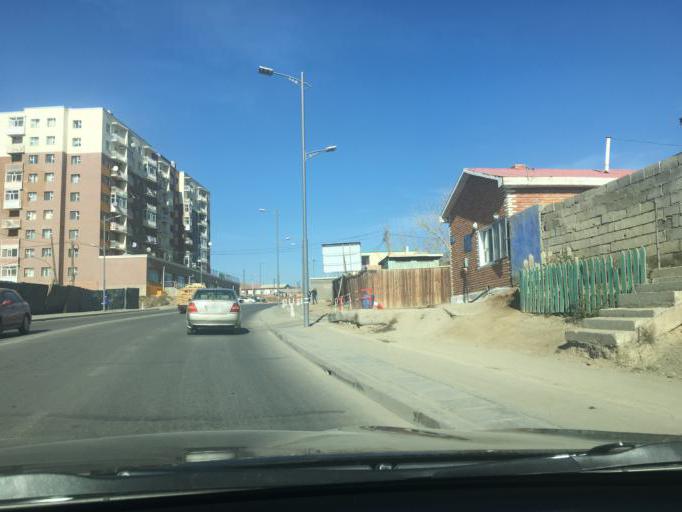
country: MN
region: Ulaanbaatar
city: Ulaanbaatar
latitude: 47.9148
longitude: 106.7809
